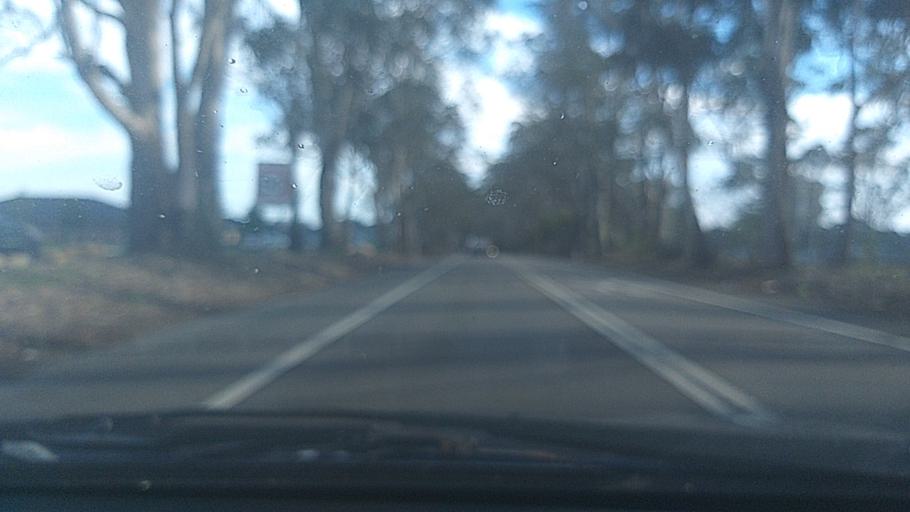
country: AU
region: New South Wales
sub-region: Wollondilly
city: Douglas Park
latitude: -34.1911
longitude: 150.7904
